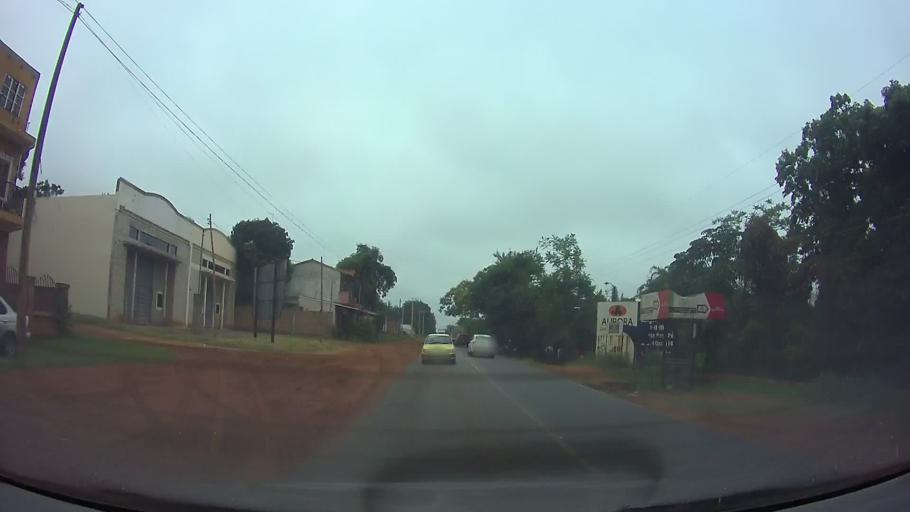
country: PY
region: Central
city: Ita
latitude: -25.4296
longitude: -57.3652
